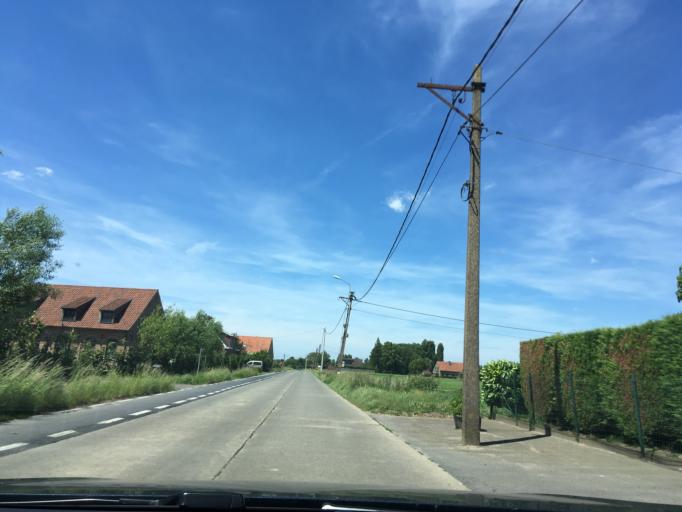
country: BE
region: Flanders
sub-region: Provincie West-Vlaanderen
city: Kortemark
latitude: 51.0195
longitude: 3.0709
